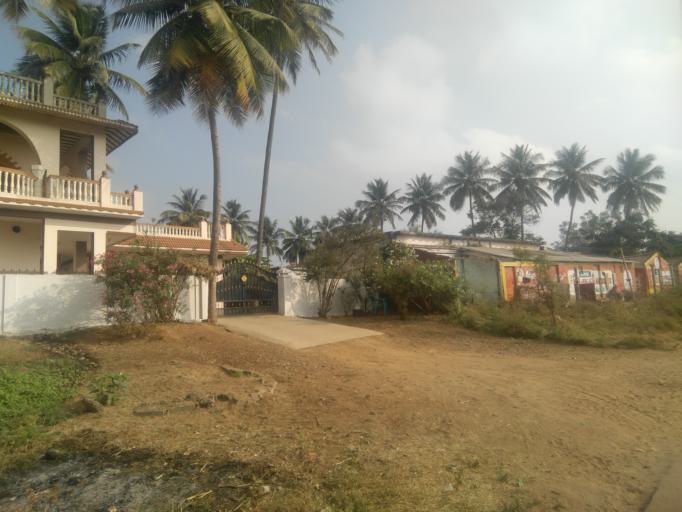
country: IN
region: Tamil Nadu
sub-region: Coimbatore
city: Coimbatore
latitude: 11.0655
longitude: 76.9157
